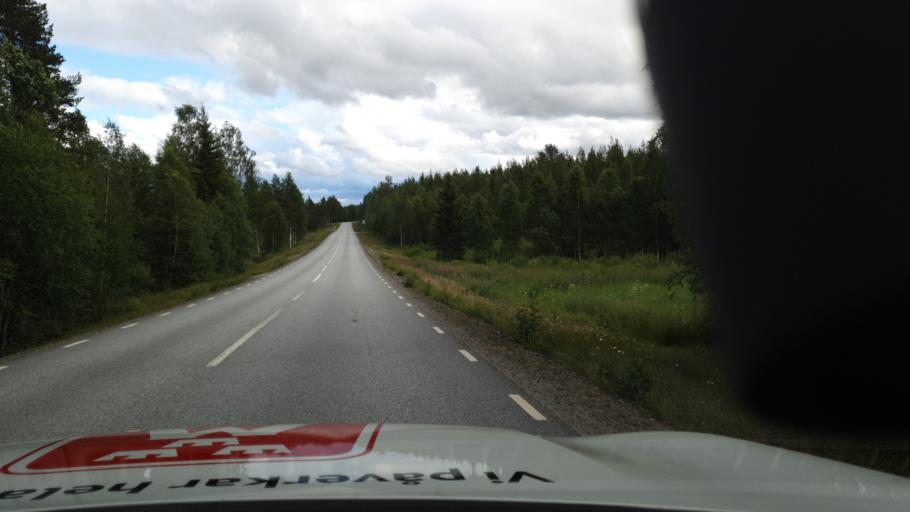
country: SE
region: Vaesterbotten
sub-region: Umea Kommun
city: Ersmark
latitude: 64.2770
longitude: 20.2267
